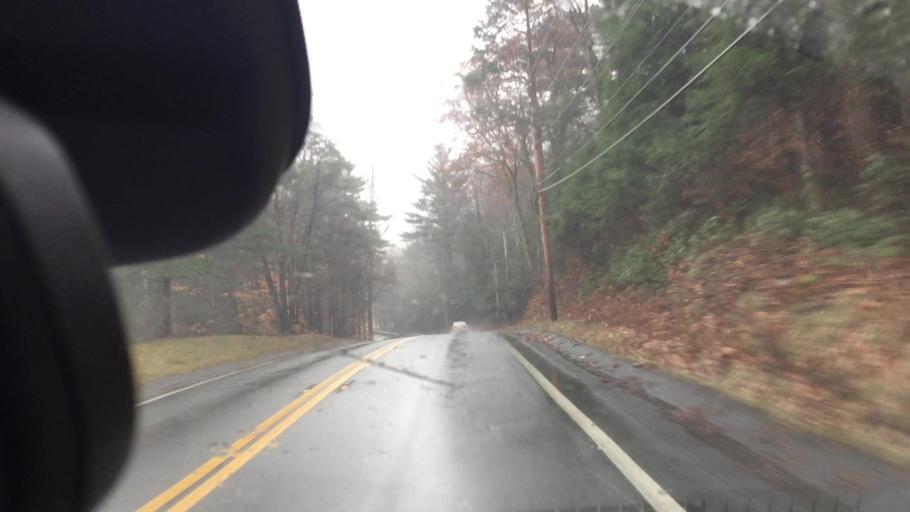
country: US
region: Massachusetts
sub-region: Hampden County
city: Granville
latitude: 42.1700
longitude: -72.8989
